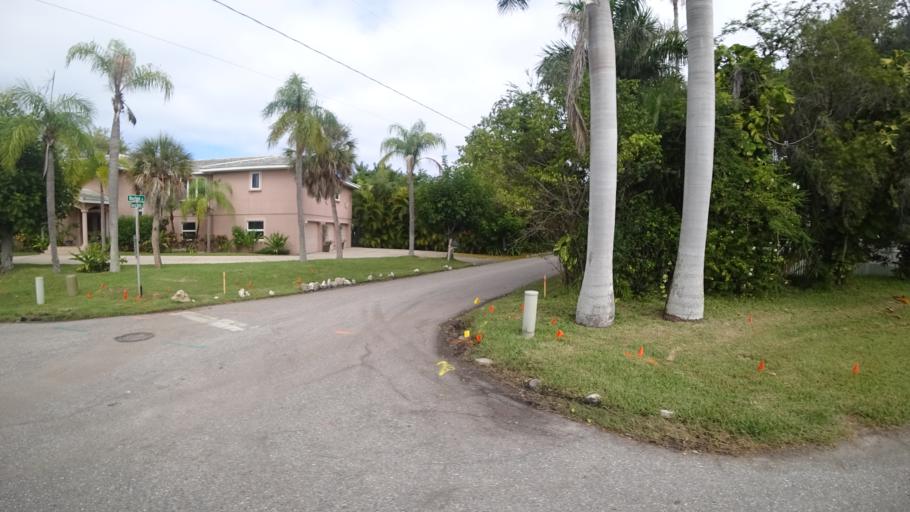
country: US
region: Florida
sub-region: Manatee County
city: Longboat Key
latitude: 27.4267
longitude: -82.6740
